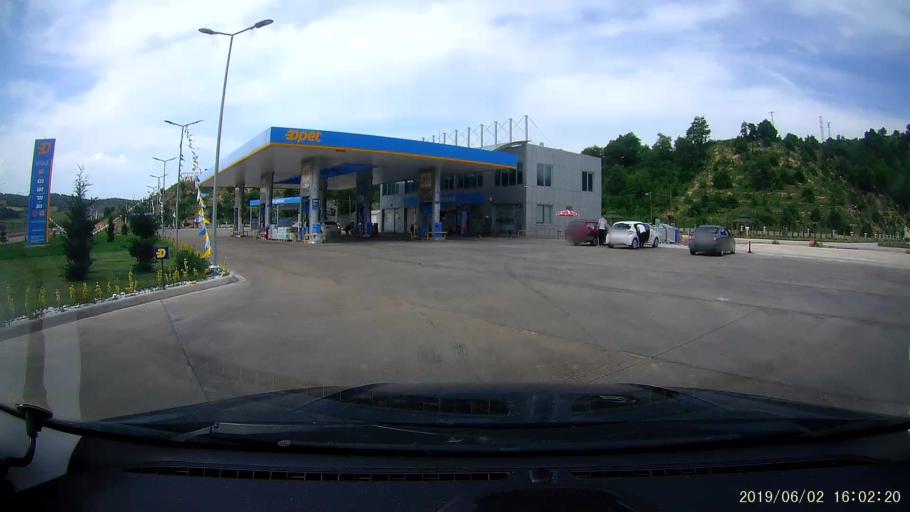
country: TR
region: Samsun
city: Havza
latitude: 40.9418
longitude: 35.6585
